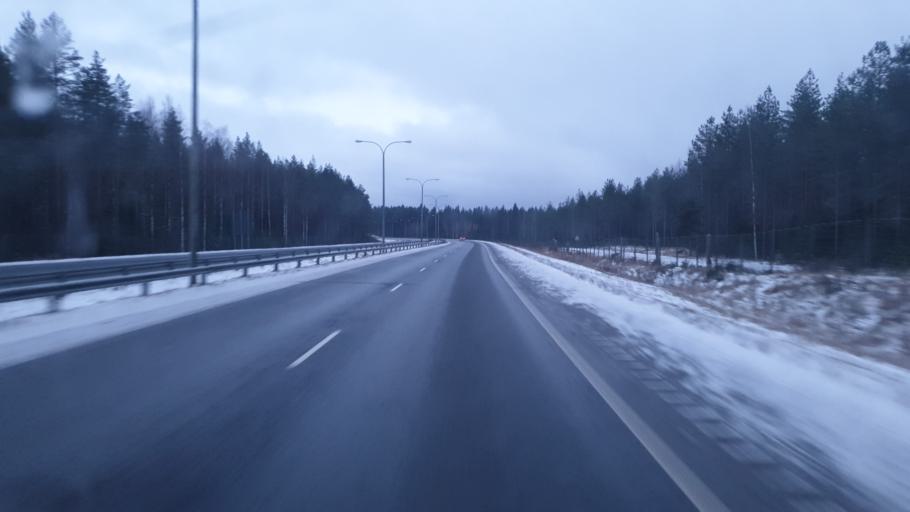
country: FI
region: Northern Savo
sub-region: Kuopio
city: Siilinjaervi
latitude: 63.0080
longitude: 27.6798
